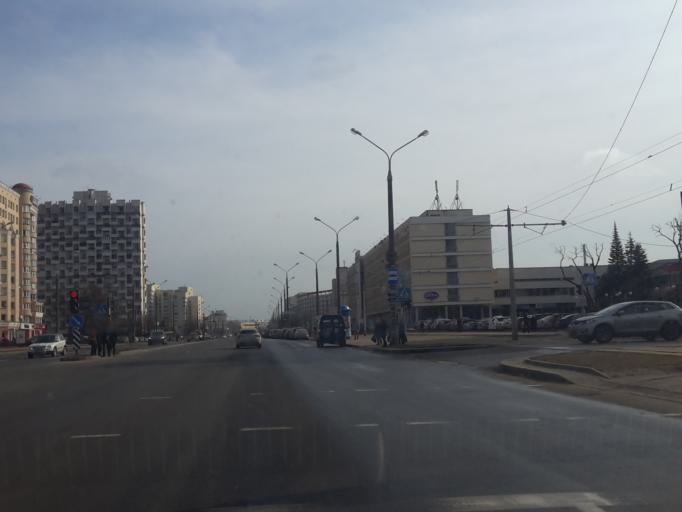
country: BY
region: Minsk
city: Minsk
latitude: 53.9175
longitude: 27.5563
